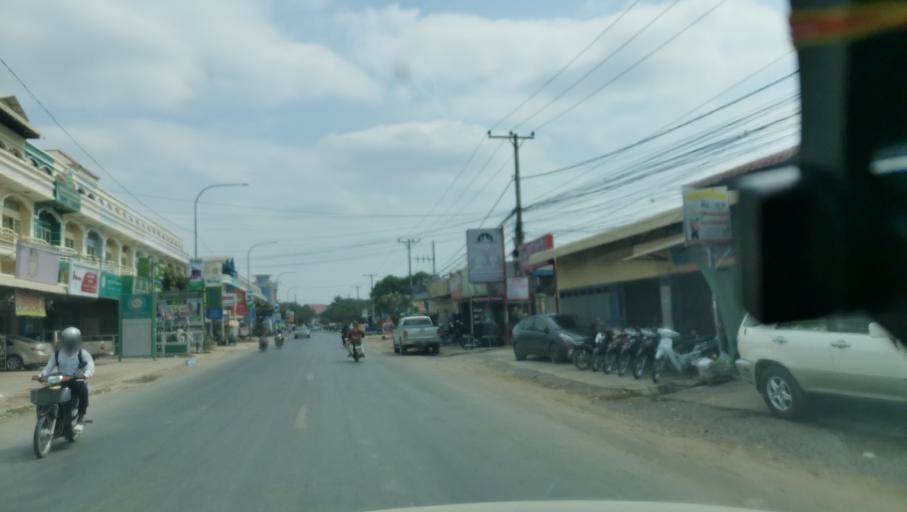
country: KH
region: Battambang
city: Battambang
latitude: 13.0845
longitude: 103.1945
